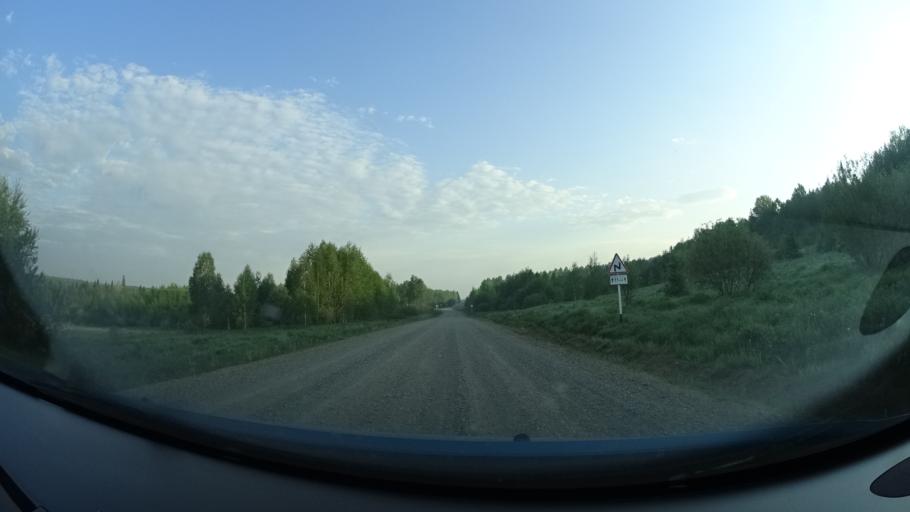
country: RU
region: Perm
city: Barda
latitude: 56.7052
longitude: 55.6784
